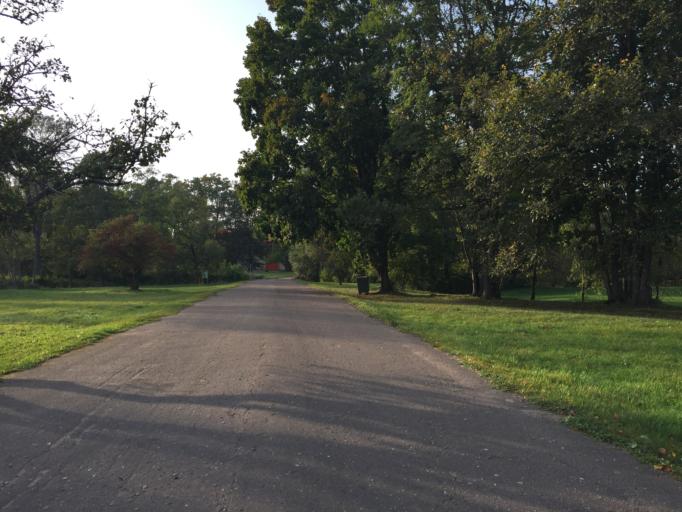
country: LV
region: Garkalne
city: Garkalne
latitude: 56.9695
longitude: 24.4917
